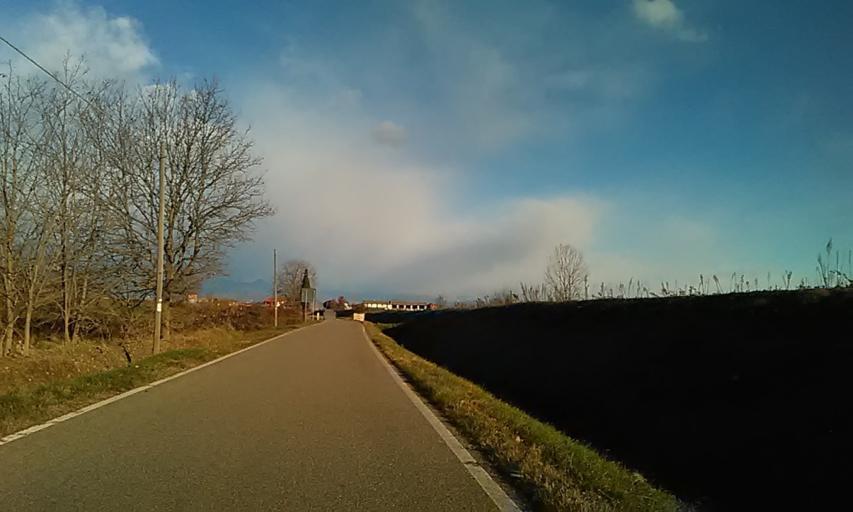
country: IT
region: Piedmont
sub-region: Provincia di Vercelli
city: Buronzo
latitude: 45.4857
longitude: 8.2720
